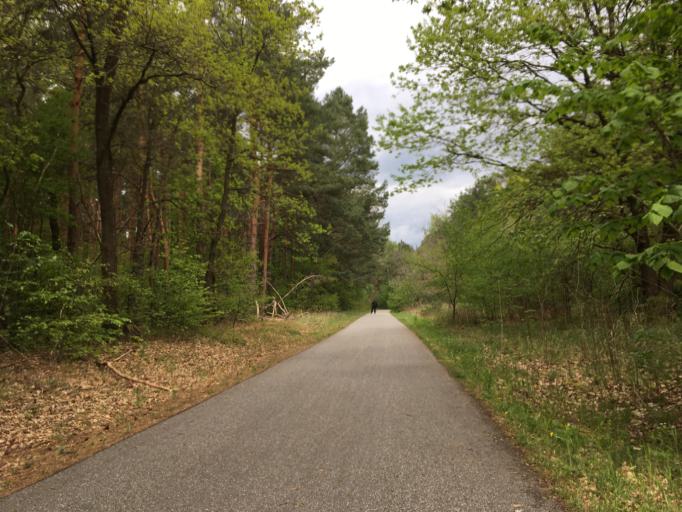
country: DE
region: Brandenburg
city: Bernau bei Berlin
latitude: 52.6882
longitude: 13.5370
